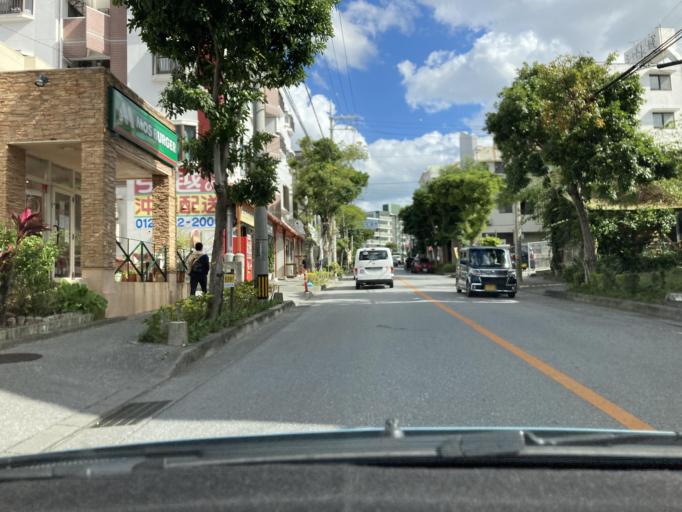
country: JP
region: Okinawa
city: Naha-shi
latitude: 26.2108
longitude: 127.6954
